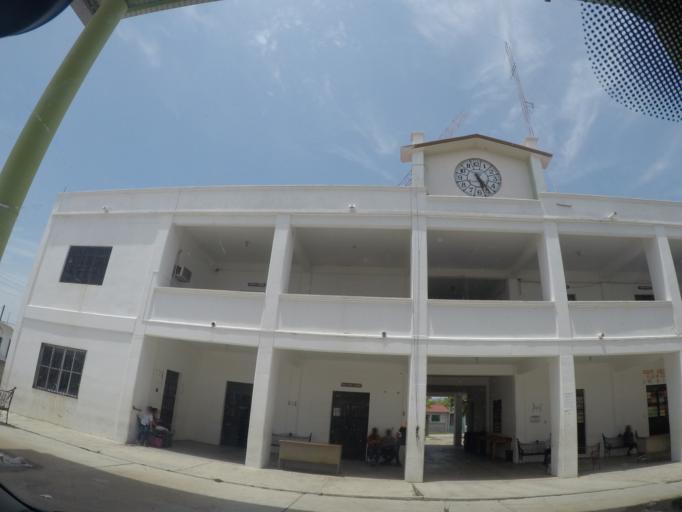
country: MX
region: Oaxaca
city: San Mateo del Mar
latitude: 16.2098
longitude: -94.9819
